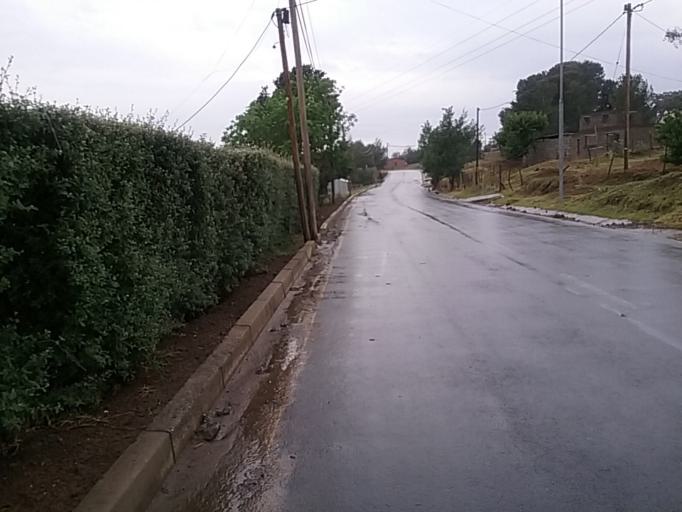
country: LS
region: Berea
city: Teyateyaneng
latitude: -29.1420
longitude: 27.7393
